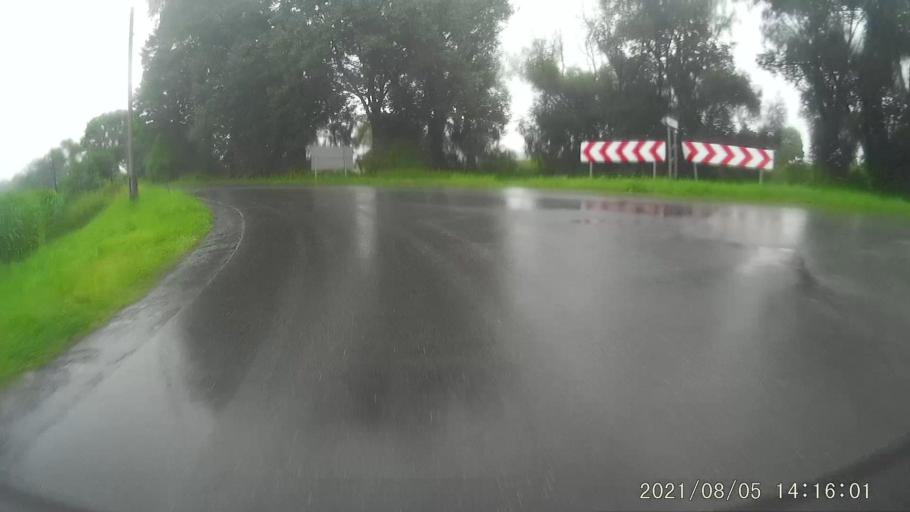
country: PL
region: Opole Voivodeship
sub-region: Powiat prudnicki
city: Biala
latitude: 50.4590
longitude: 17.7279
